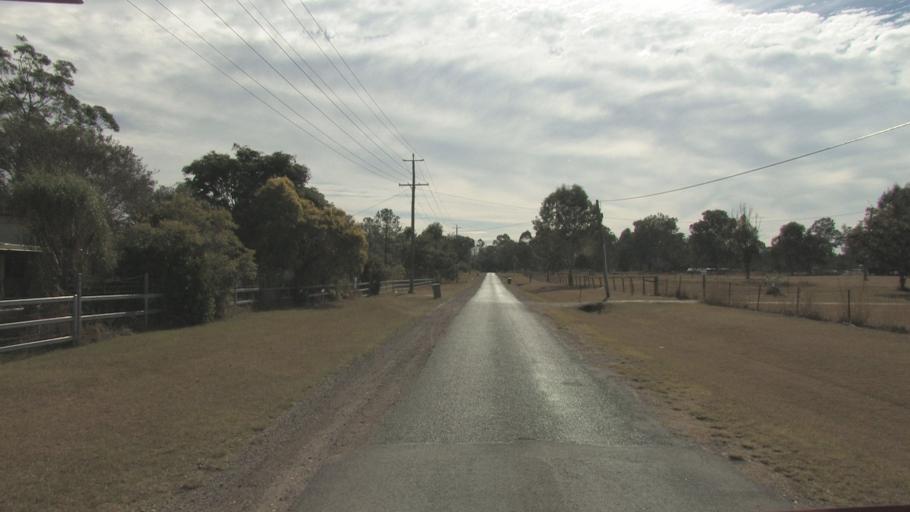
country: AU
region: Queensland
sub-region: Logan
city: North Maclean
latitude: -27.7785
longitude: 153.0080
